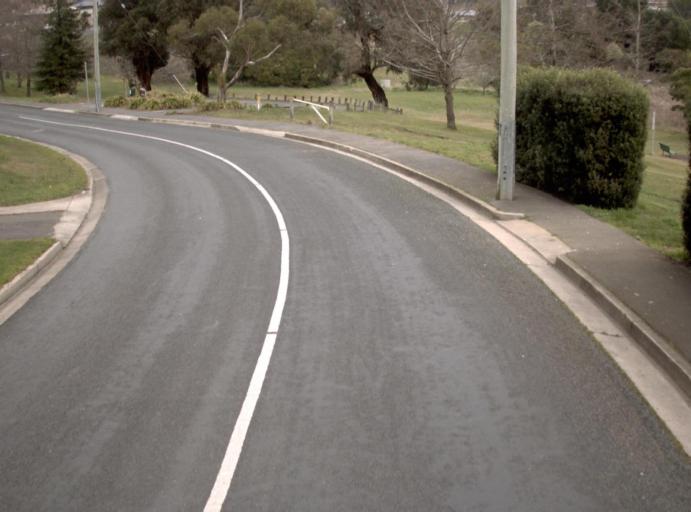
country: AU
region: Tasmania
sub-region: Launceston
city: Newstead
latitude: -41.4507
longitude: 147.1739
